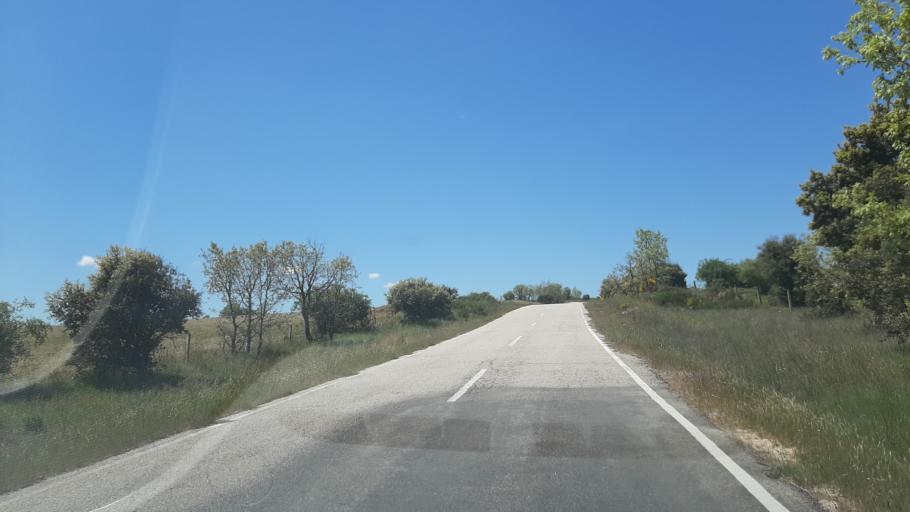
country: ES
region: Castille and Leon
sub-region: Provincia de Salamanca
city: Vitigudino
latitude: 41.0291
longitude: -6.4057
